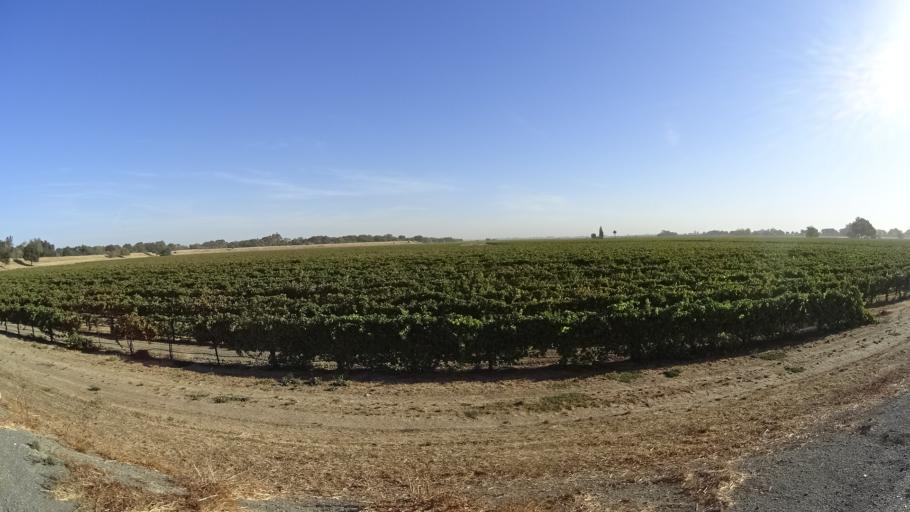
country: US
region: California
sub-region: Sacramento County
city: Walnut Grove
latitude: 38.3409
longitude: -121.5792
